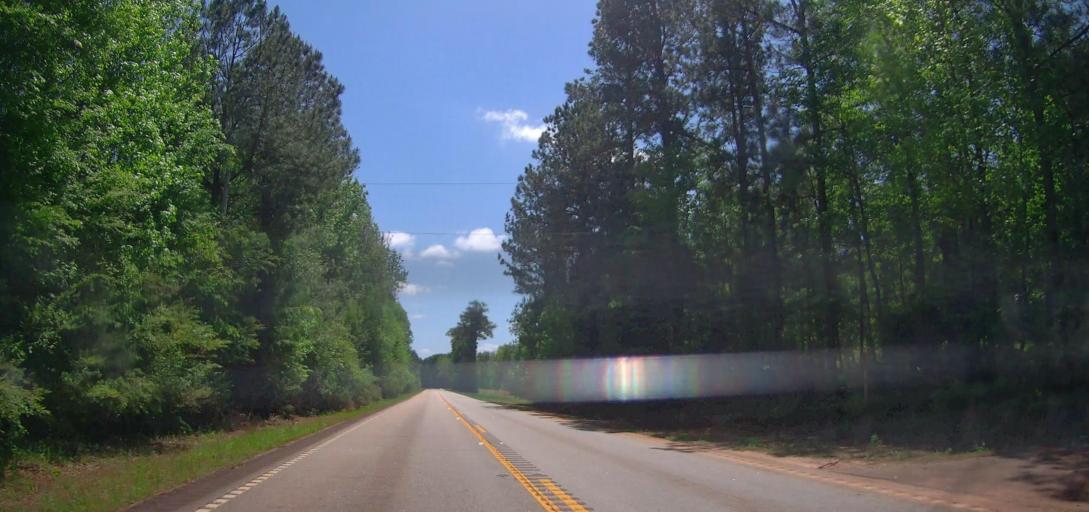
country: US
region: Georgia
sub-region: Jasper County
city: Monticello
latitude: 33.1973
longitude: -83.6560
